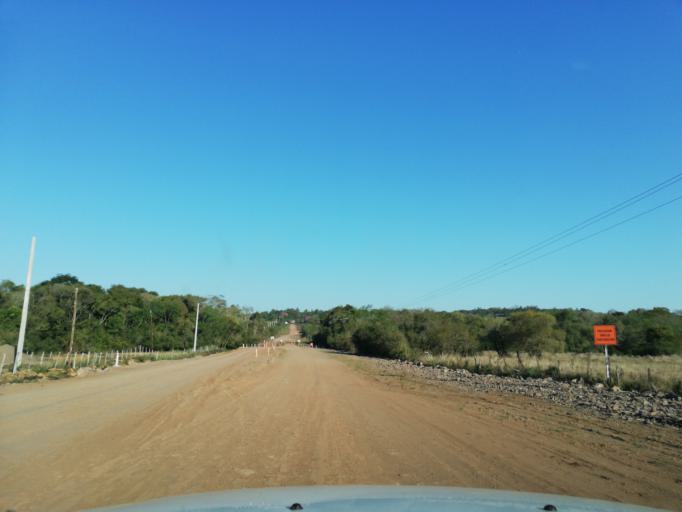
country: AR
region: Misiones
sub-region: Departamento de Candelaria
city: Candelaria
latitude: -27.5337
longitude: -55.7179
